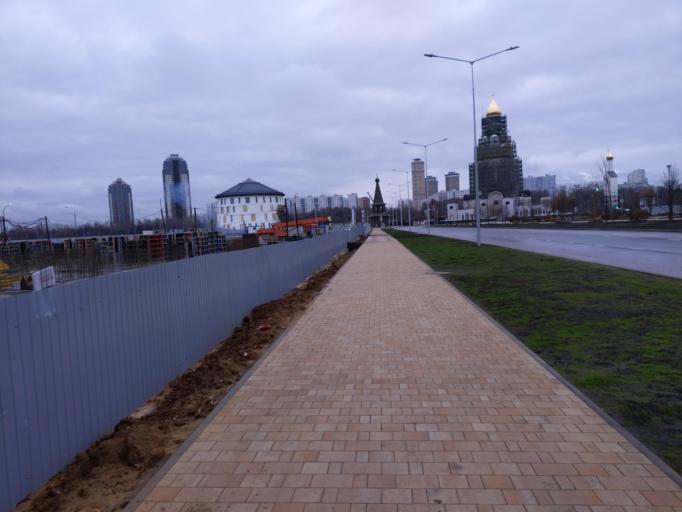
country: RU
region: Moscow
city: Strogino
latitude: 55.8149
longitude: 37.4242
